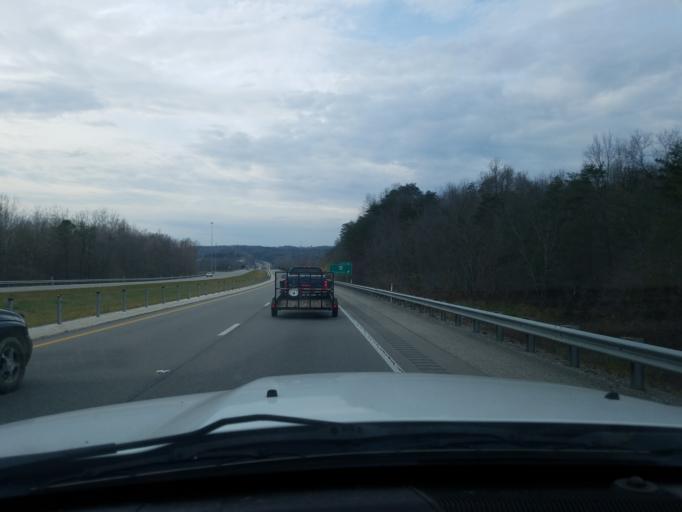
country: US
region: Kentucky
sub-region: Carter County
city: Olive Hill
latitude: 38.3256
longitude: -83.1108
